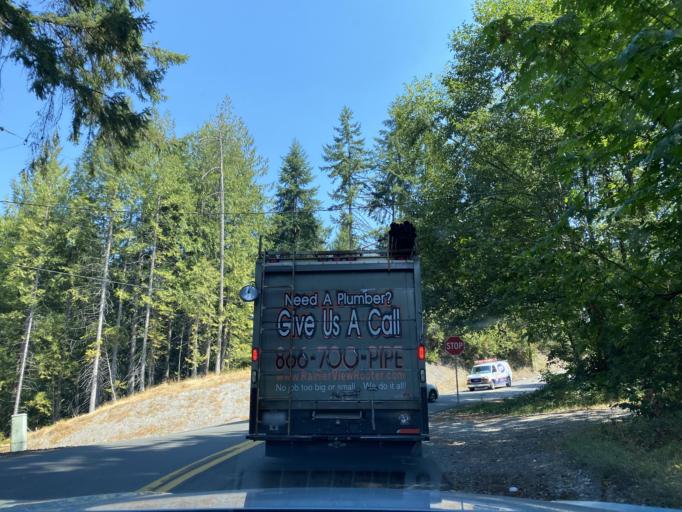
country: US
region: Washington
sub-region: Pierce County
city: Alderton
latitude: 47.1559
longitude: -122.2112
